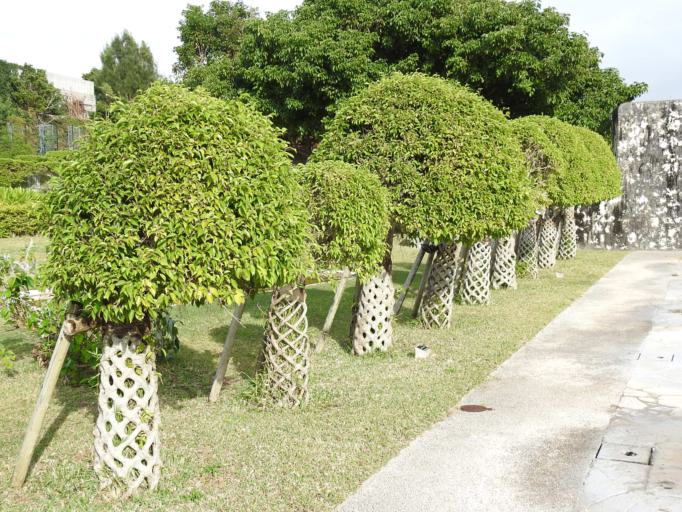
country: JP
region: Okinawa
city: Nago
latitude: 26.6809
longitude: 127.8825
